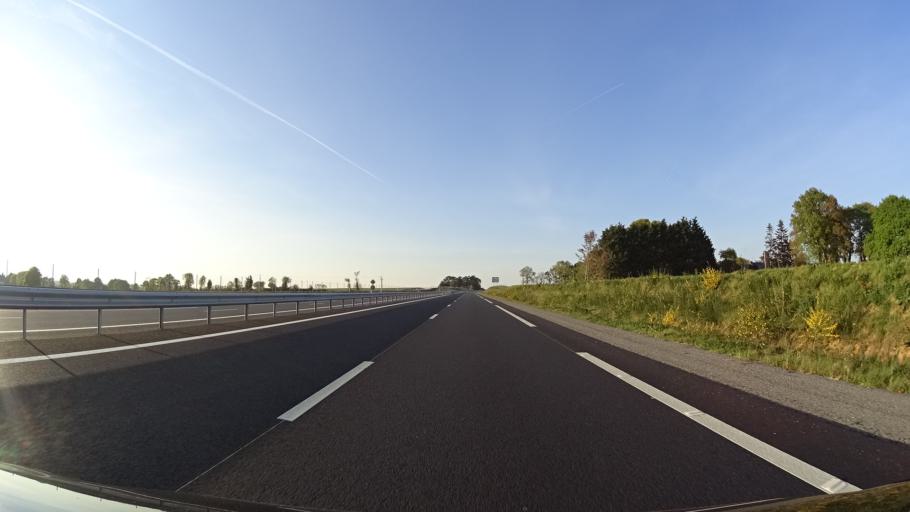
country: FR
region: Brittany
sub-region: Departement d'Ille-et-Vilaine
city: Pipriac
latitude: 47.8089
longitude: -1.9203
